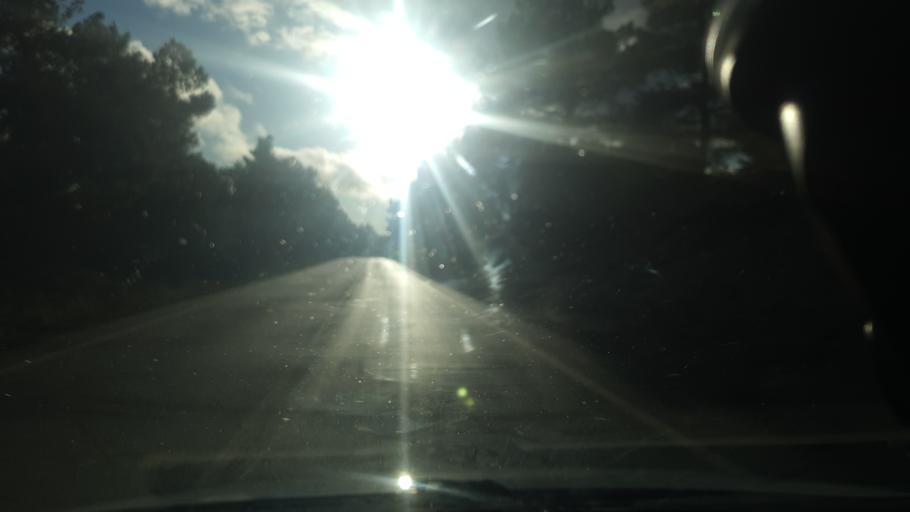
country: ES
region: Castille and Leon
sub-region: Provincia de Segovia
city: Santiuste de San Juan Bautista
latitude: 41.1512
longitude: -4.5383
